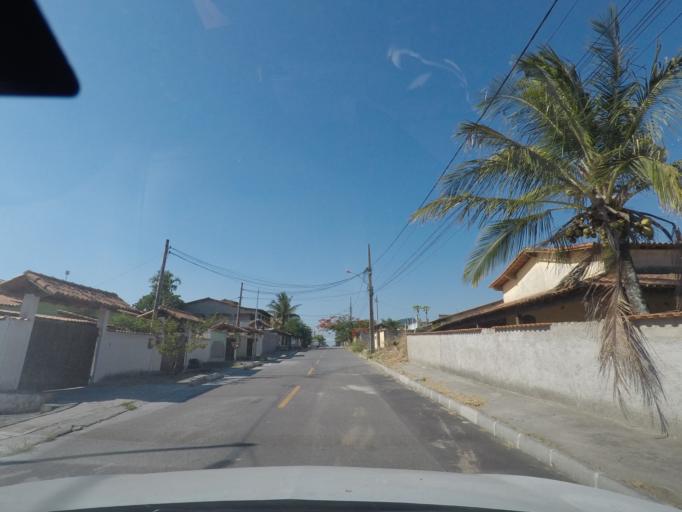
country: BR
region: Rio de Janeiro
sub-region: Marica
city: Marica
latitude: -22.9715
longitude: -42.9217
